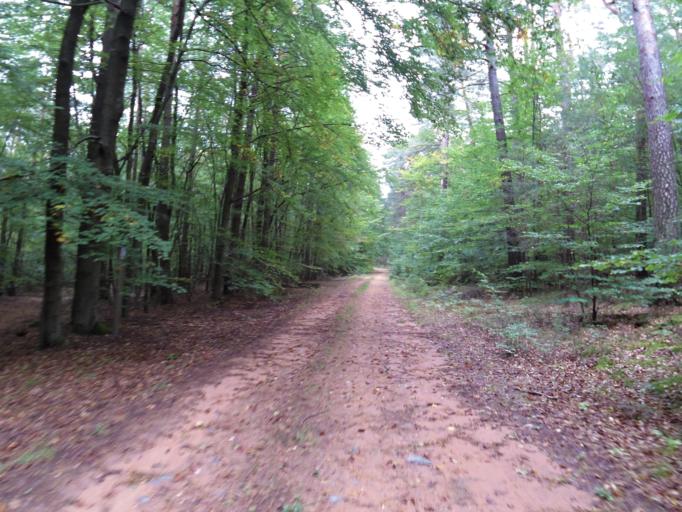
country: DE
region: Rheinland-Pfalz
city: Neuhemsbach
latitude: 49.4973
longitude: 7.9426
